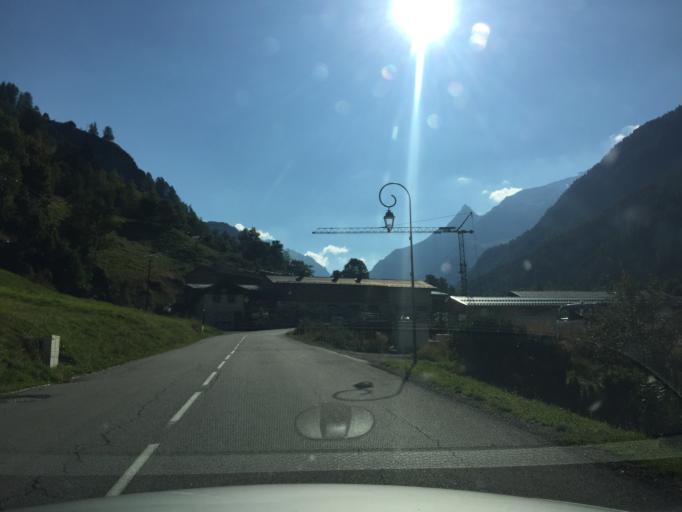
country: FR
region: Rhone-Alpes
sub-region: Departement de la Savoie
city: Belle-Plagne
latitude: 45.5397
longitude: 6.7609
